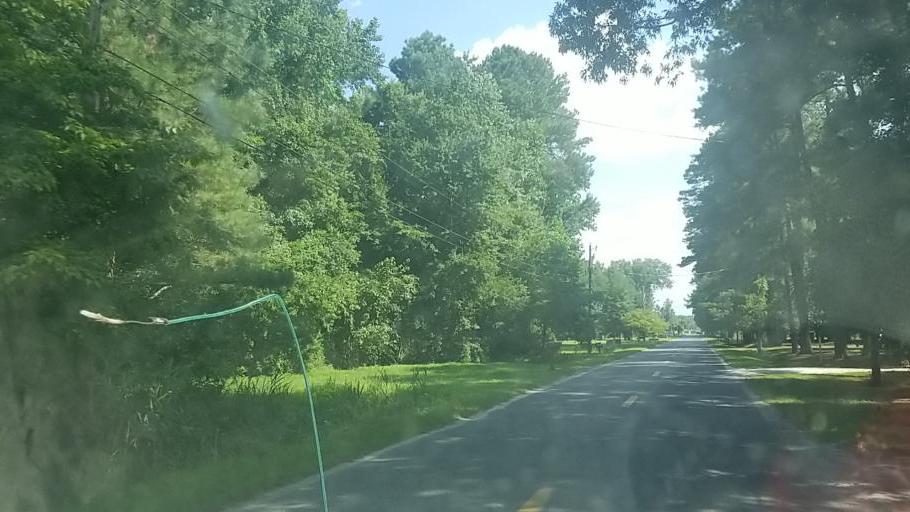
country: US
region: Maryland
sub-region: Wicomico County
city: Fruitland
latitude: 38.3128
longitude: -75.6329
